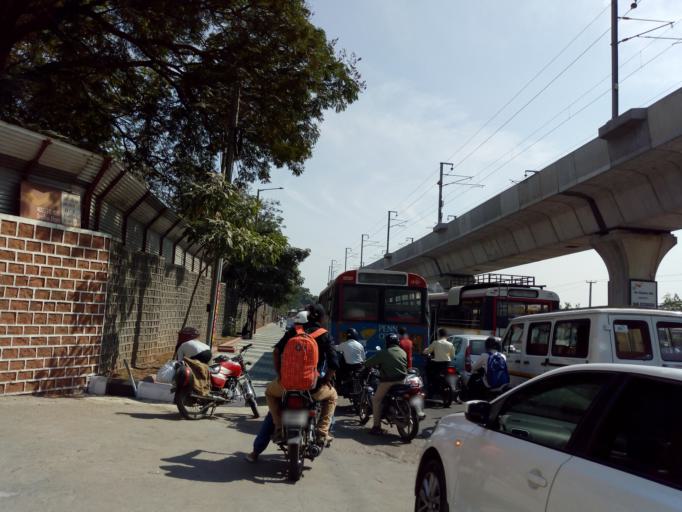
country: IN
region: Telangana
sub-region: Rangareddi
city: Uppal Kalan
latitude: 17.4225
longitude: 78.5384
